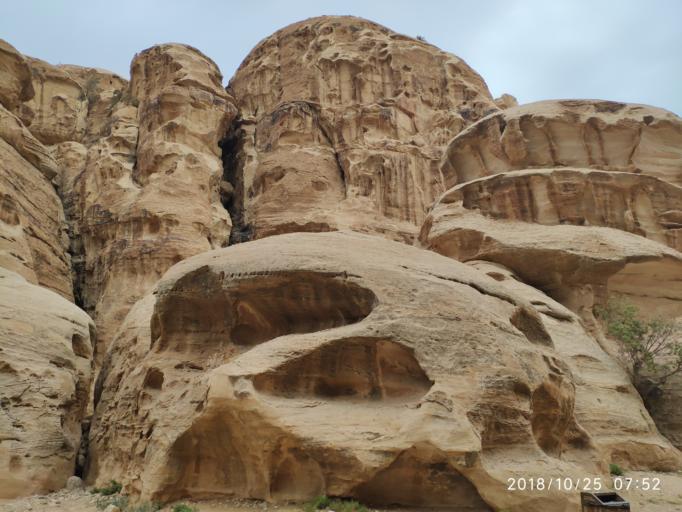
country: JO
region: Ma'an
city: Petra
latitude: 30.3749
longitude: 35.4506
